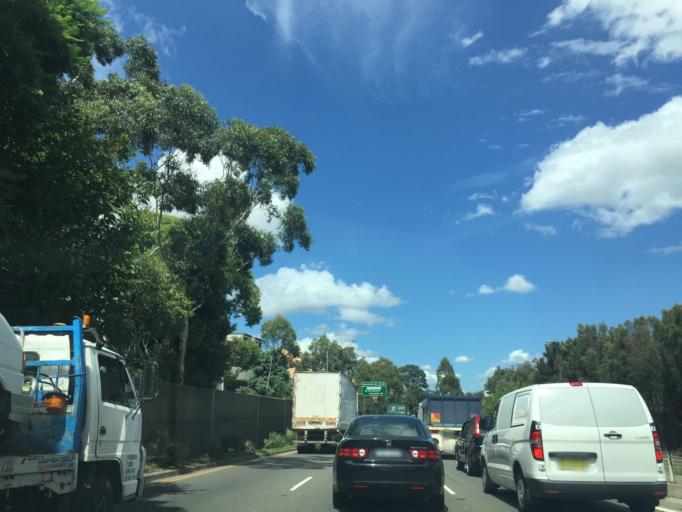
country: AU
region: New South Wales
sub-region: Strathfield
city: Homebush
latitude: -33.8651
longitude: 151.0660
